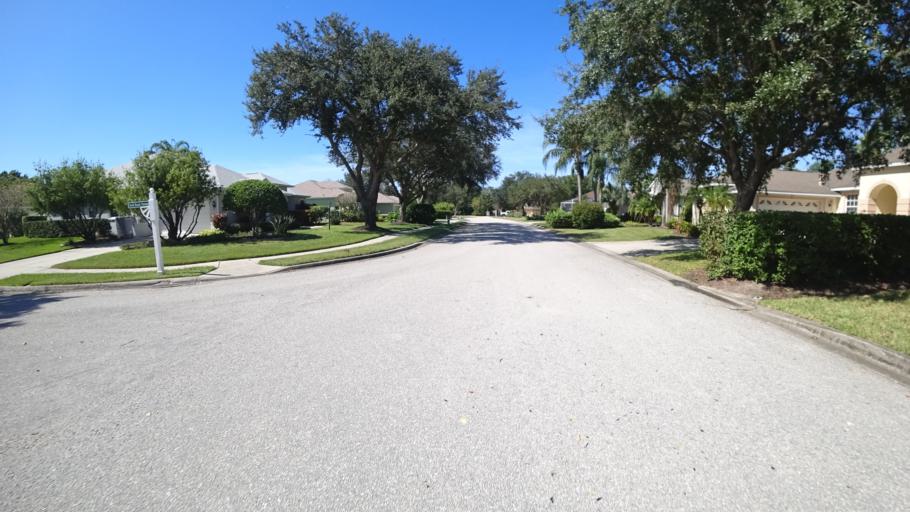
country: US
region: Florida
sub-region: Sarasota County
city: The Meadows
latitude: 27.4234
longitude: -82.4222
